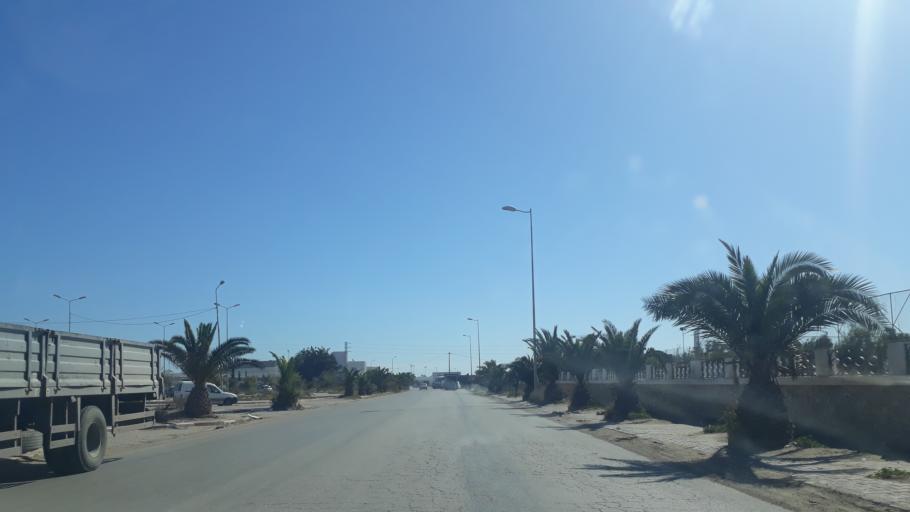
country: TN
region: Safaqis
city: Sfax
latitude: 34.7271
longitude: 10.7531
